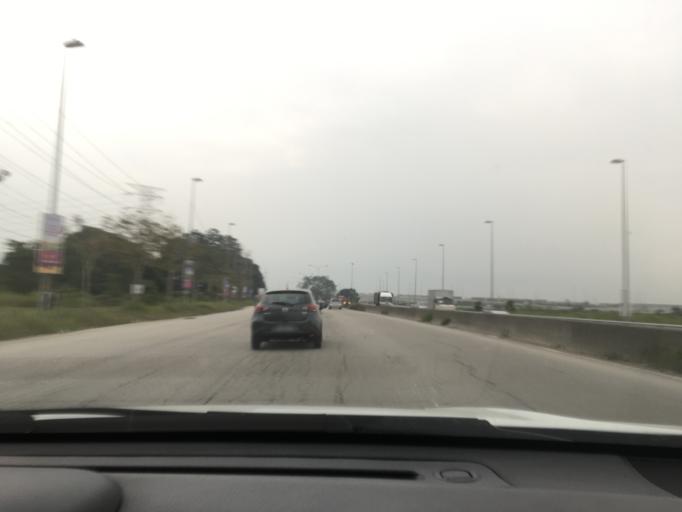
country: MY
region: Selangor
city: Klang
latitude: 3.0958
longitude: 101.4432
